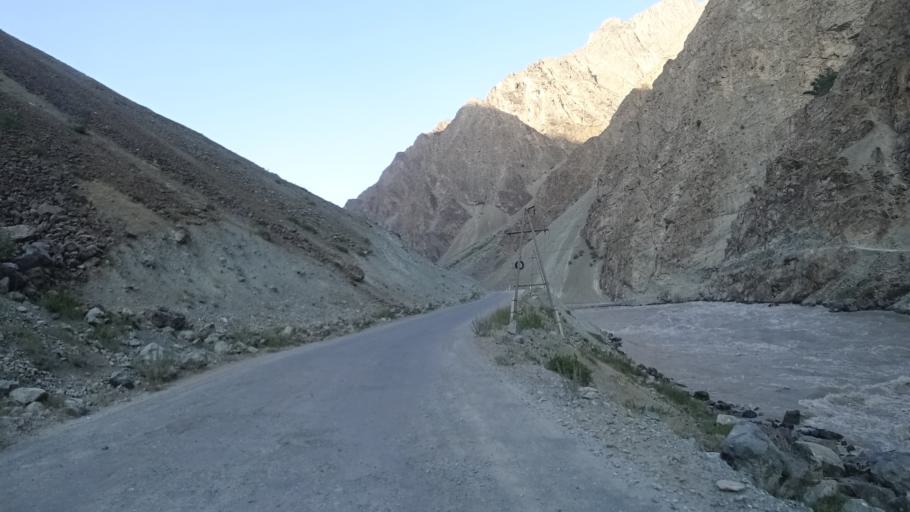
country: TJ
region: Gorno-Badakhshan
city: Qalaikhumb
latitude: 38.4261
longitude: 70.7515
